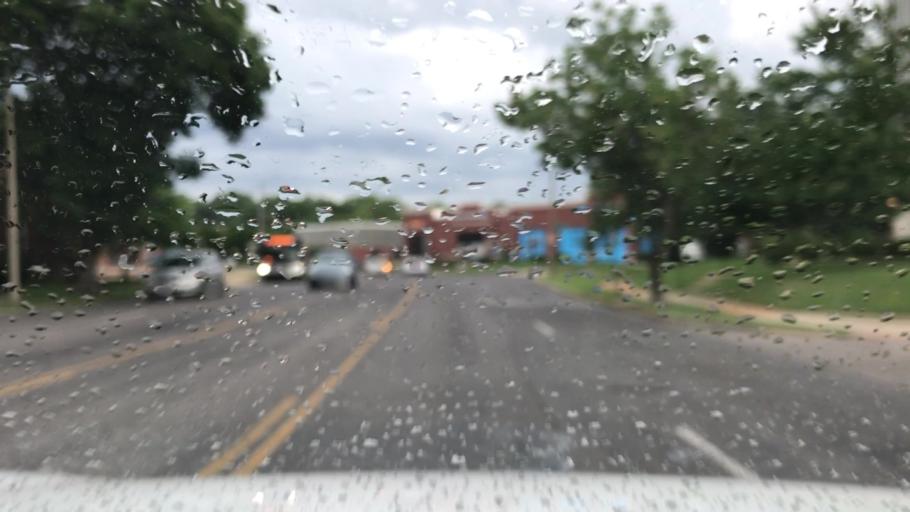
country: US
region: Missouri
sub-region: Saint Louis County
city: Maplewood
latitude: 38.5938
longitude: -90.2971
